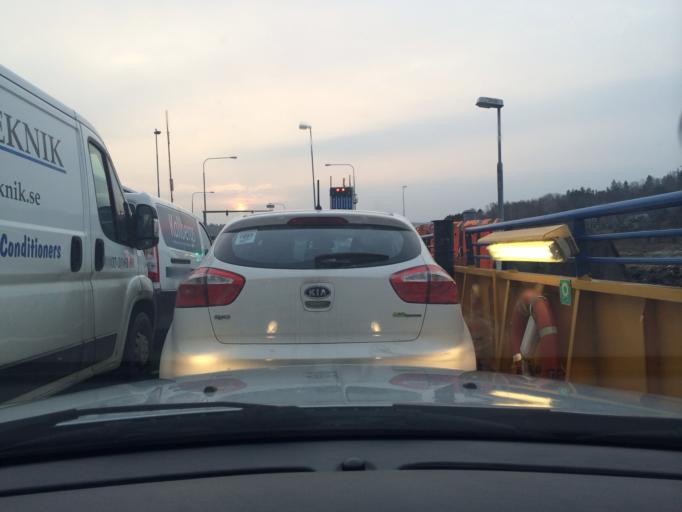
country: SE
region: Vaestra Goetaland
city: Svanesund
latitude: 58.1344
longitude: 11.8426
